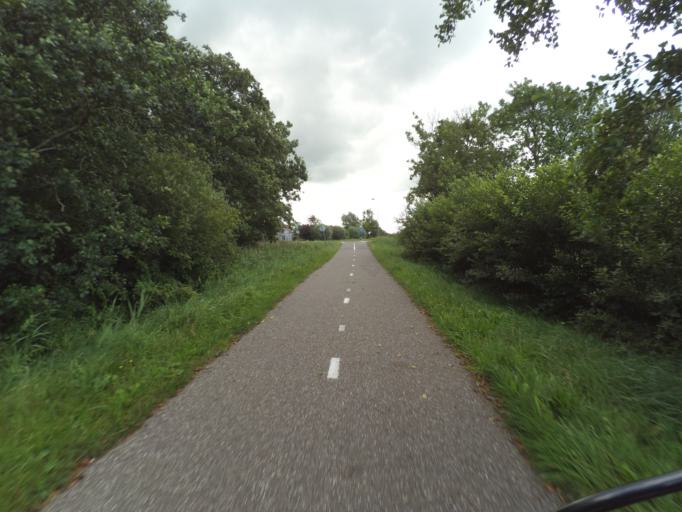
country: NL
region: Friesland
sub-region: Gemeente Tytsjerksteradiel
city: Hurdegaryp
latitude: 53.2078
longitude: 5.9433
